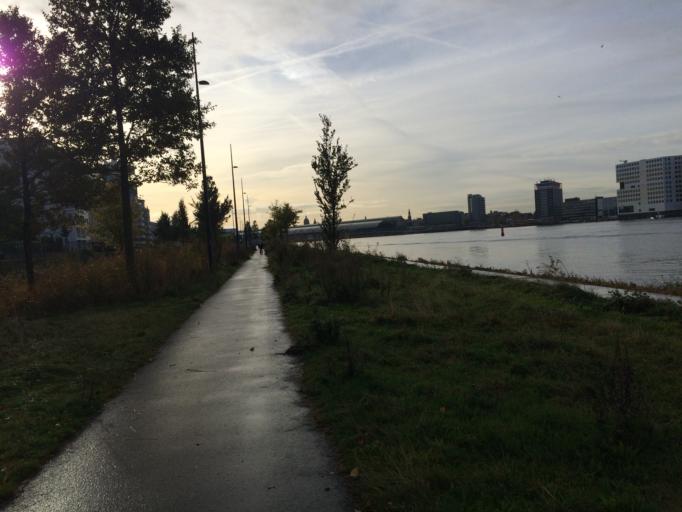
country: NL
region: North Holland
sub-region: Gemeente Amsterdam
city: Amsterdam
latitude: 52.3885
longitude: 4.8987
